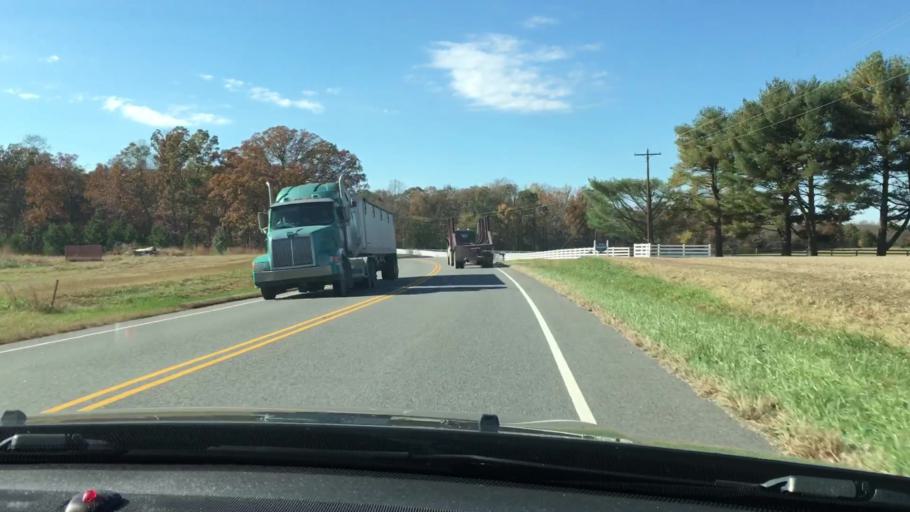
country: US
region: Virginia
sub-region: King William County
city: Central Garage
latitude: 37.7910
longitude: -77.2008
